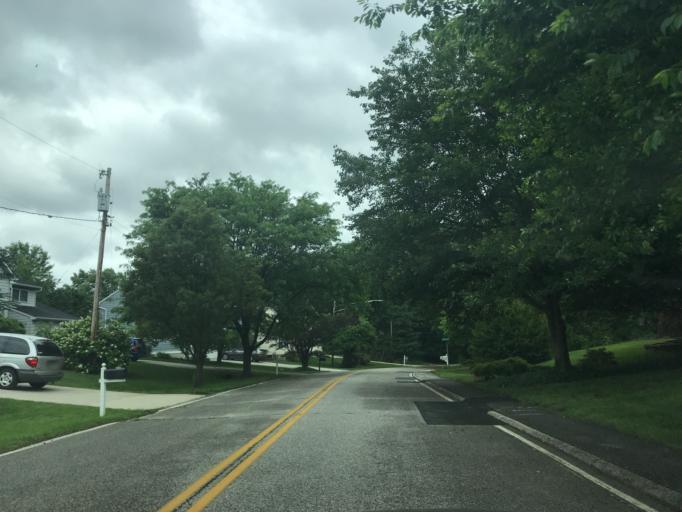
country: US
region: Maryland
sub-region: Anne Arundel County
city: Linthicum
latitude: 39.2068
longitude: -76.6566
